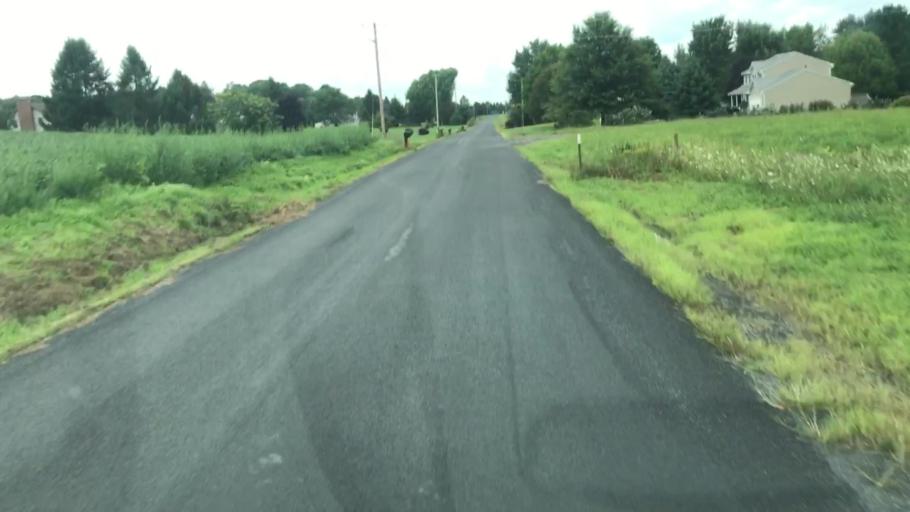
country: US
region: New York
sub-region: Cayuga County
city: Auburn
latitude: 42.9730
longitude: -76.5087
